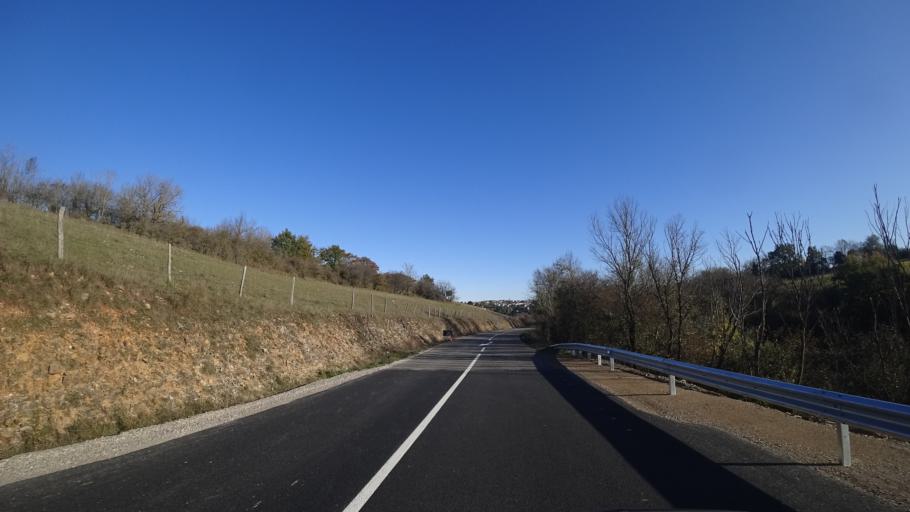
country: FR
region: Midi-Pyrenees
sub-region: Departement de l'Aveyron
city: Rodez
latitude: 44.3809
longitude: 2.5558
